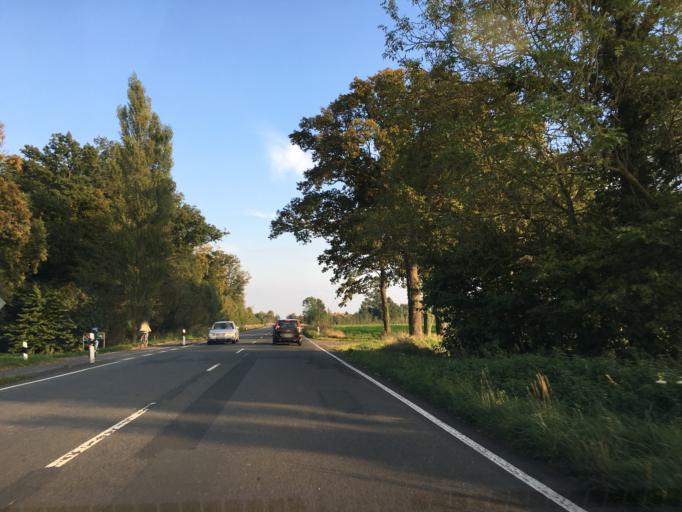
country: DE
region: North Rhine-Westphalia
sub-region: Regierungsbezirk Munster
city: Altenberge
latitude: 52.0136
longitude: 7.5193
